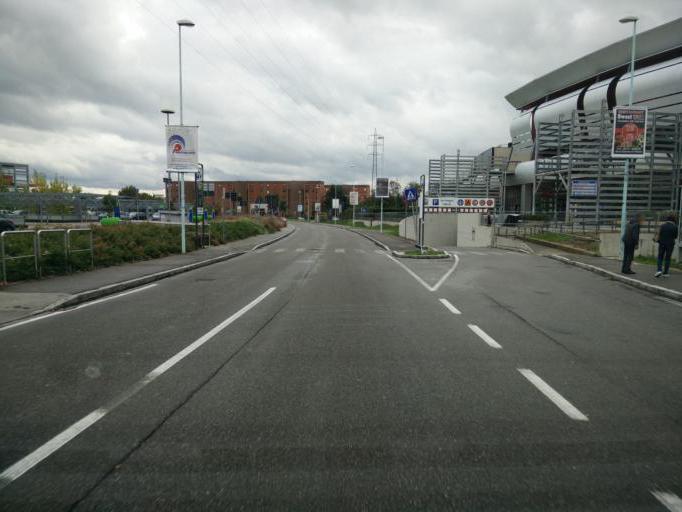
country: IT
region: Tuscany
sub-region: Provincia di Prato
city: Prato
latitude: 43.8742
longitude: 11.0636
